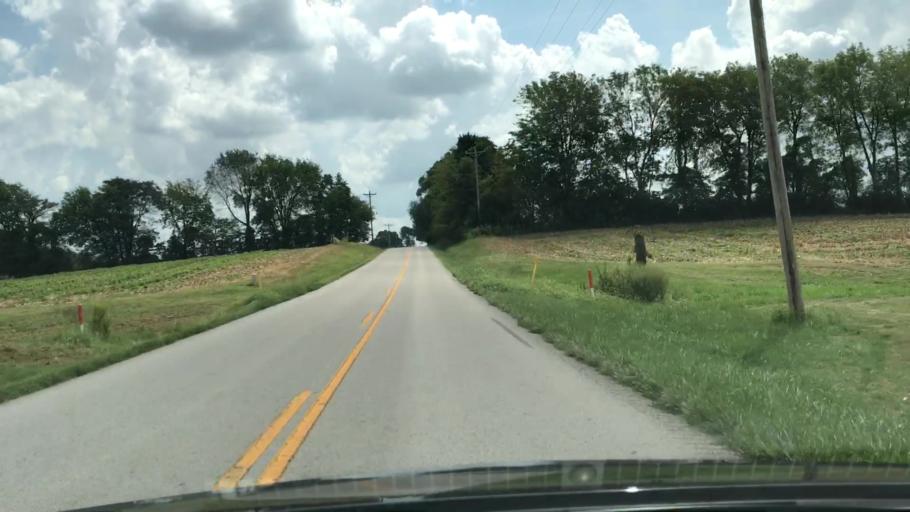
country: US
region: Kentucky
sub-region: Todd County
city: Elkton
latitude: 36.7834
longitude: -87.1262
